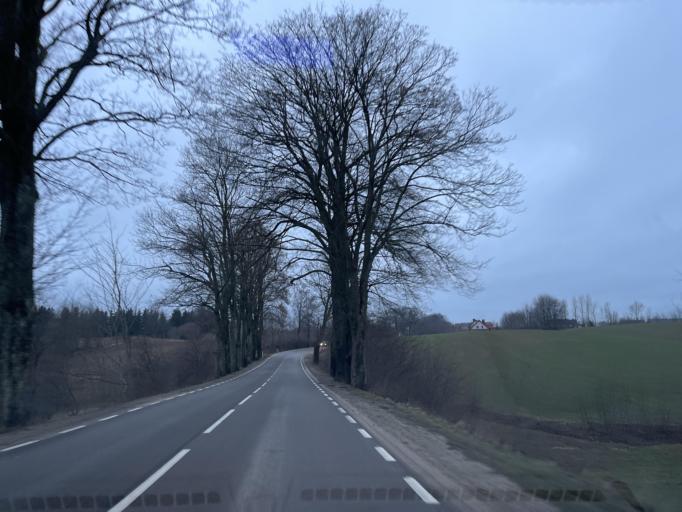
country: PL
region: Pomeranian Voivodeship
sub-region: Powiat kartuski
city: Przodkowo
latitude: 54.3973
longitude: 18.2322
